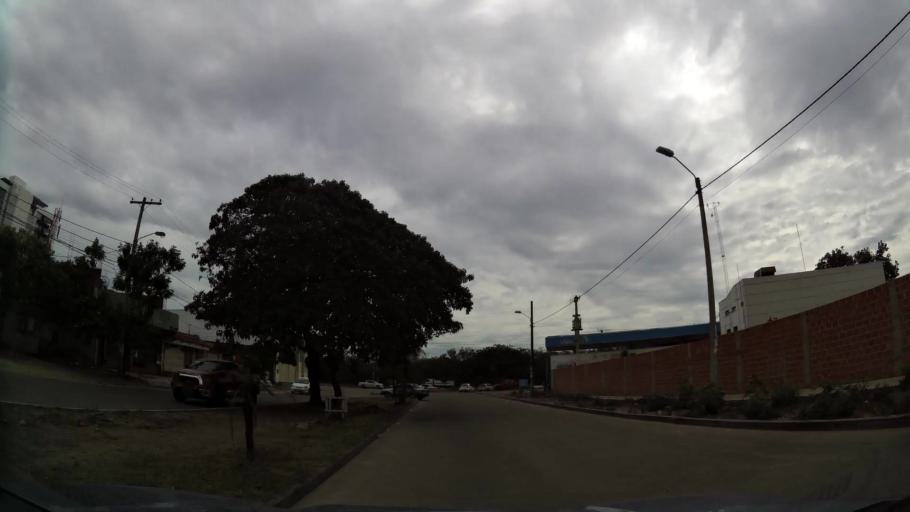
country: BO
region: Santa Cruz
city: Santa Cruz de la Sierra
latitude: -17.7778
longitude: -63.2153
